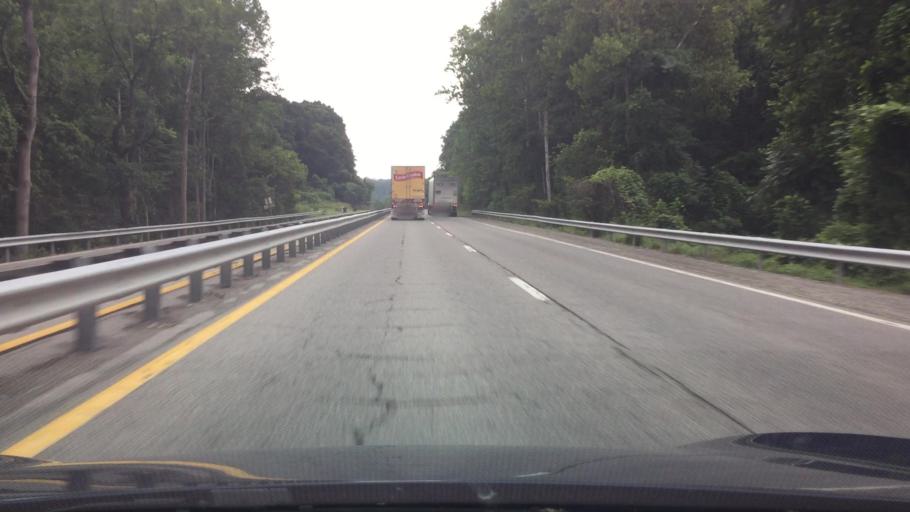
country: US
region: Virginia
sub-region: Montgomery County
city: Shawsville
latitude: 37.2389
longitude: -80.1839
